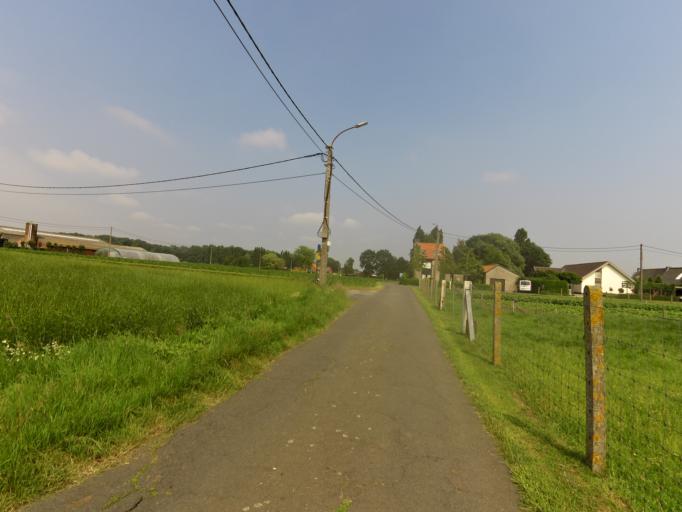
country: BE
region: Flanders
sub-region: Provincie West-Vlaanderen
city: Ichtegem
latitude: 51.1166
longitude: 3.0429
